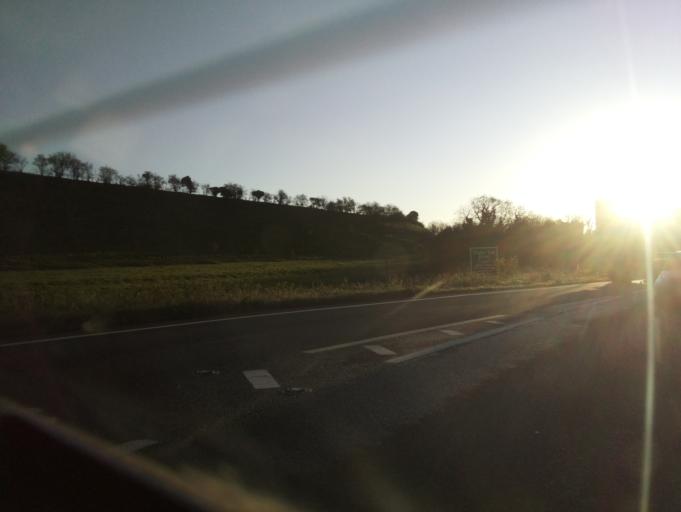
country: GB
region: England
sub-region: Wiltshire
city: Mere
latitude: 51.0967
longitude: -2.2262
